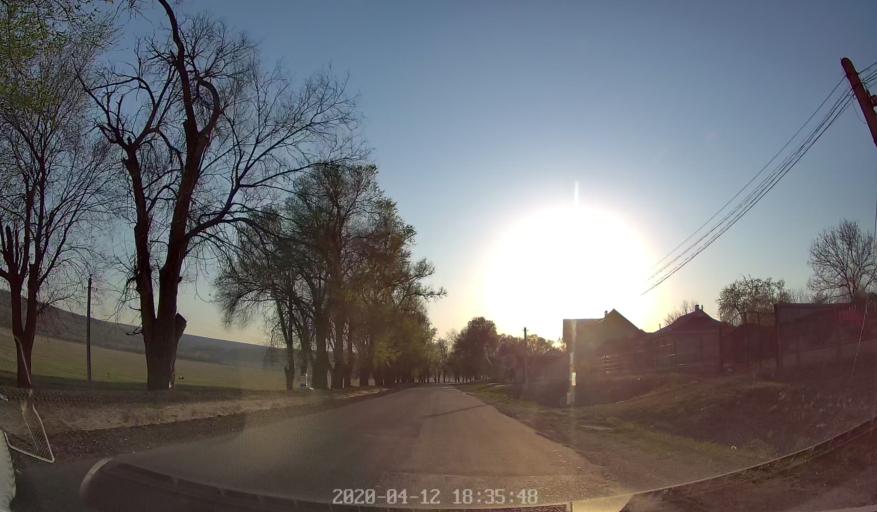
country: MD
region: Chisinau
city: Vadul lui Voda
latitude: 47.1159
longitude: 29.0405
